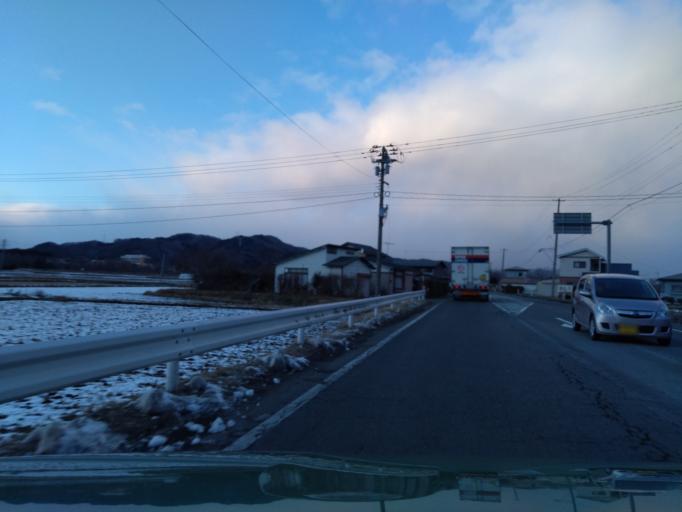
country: JP
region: Iwate
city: Shizukuishi
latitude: 39.6909
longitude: 141.0653
